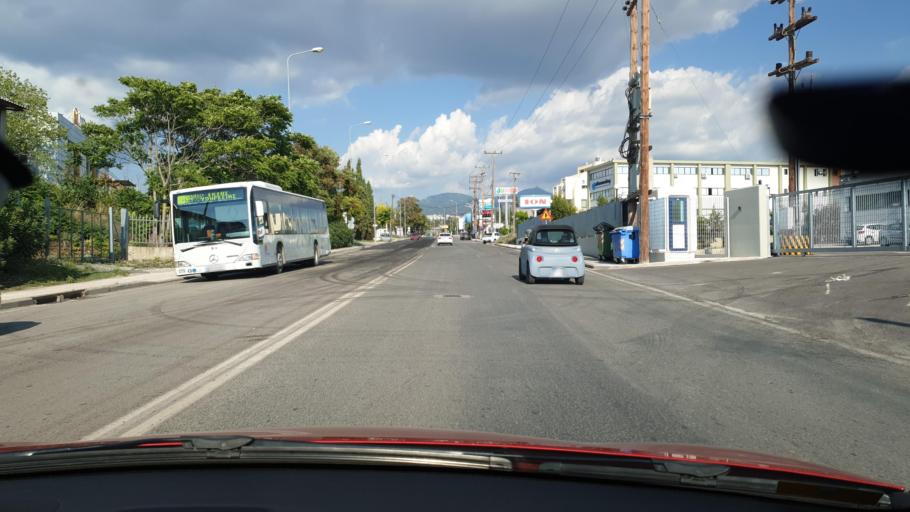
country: GR
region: Central Macedonia
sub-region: Nomos Thessalonikis
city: Pylaia
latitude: 40.5688
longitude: 22.9802
